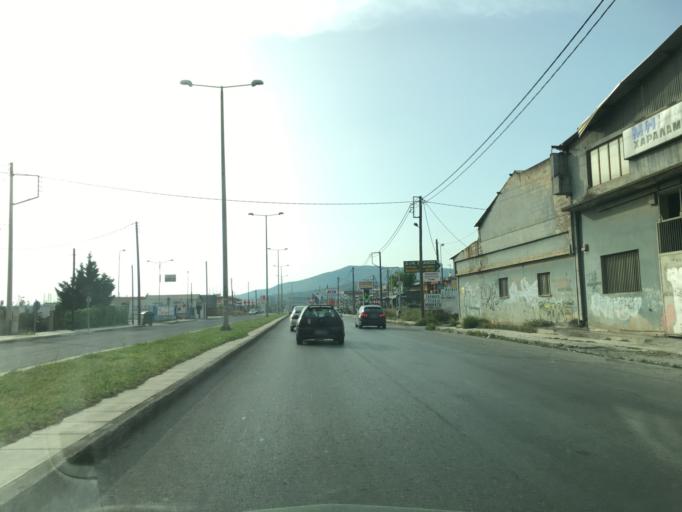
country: GR
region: Thessaly
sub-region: Nomos Magnisias
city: Nea Ionia
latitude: 39.3698
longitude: 22.9173
